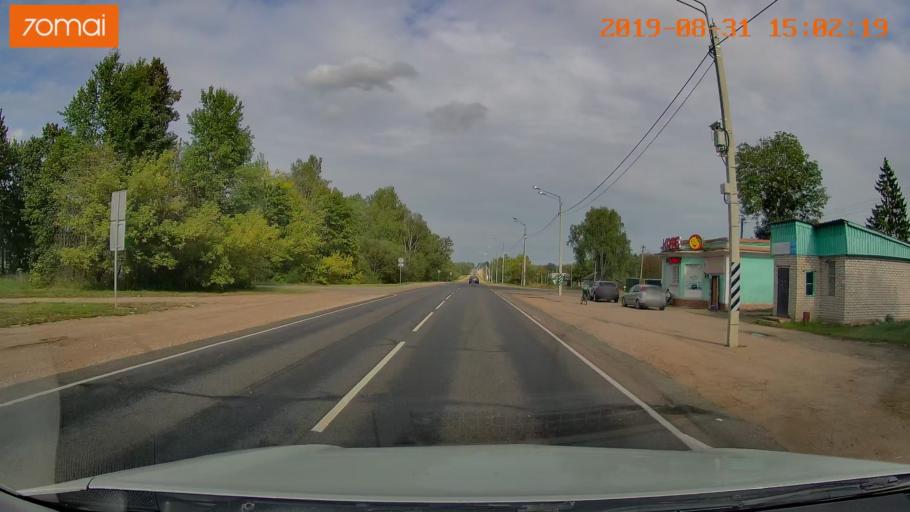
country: RU
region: Kaluga
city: Spas-Demensk
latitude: 54.3449
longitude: 34.0725
